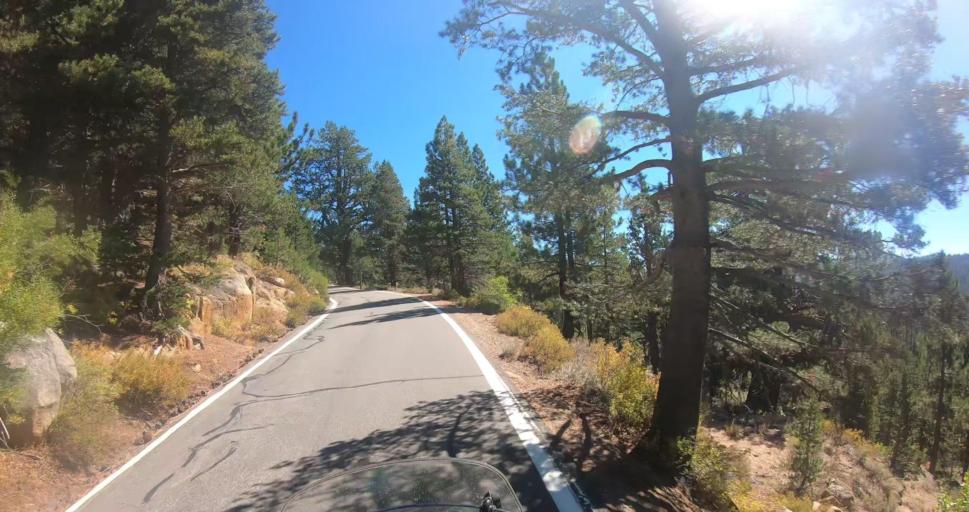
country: US
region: Nevada
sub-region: Douglas County
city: Gardnerville Ranchos
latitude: 38.5470
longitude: -119.8330
